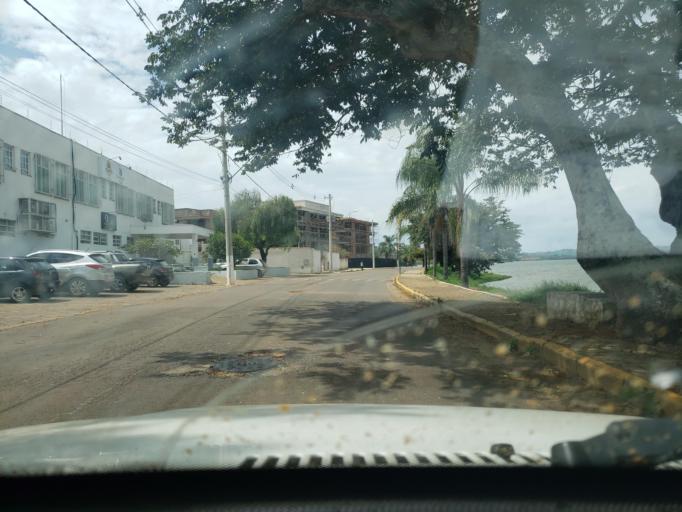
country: BR
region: Minas Gerais
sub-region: Boa Esperanca
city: Boa Esperanca
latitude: -21.0849
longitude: -45.5704
